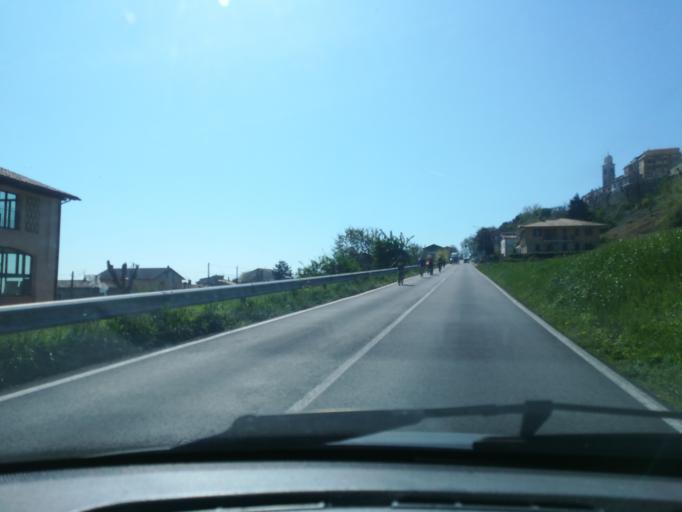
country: IT
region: The Marches
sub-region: Provincia di Macerata
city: Cingoli
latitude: 43.3776
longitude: 13.2167
